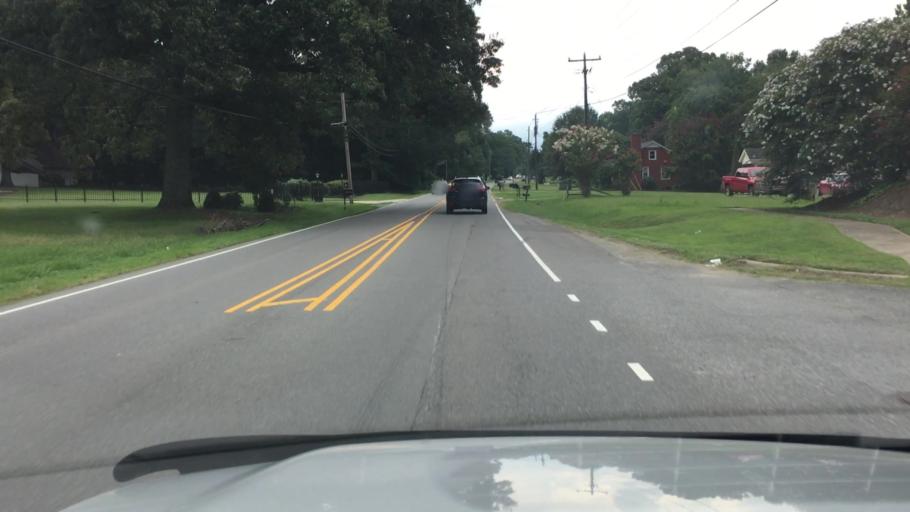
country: US
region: North Carolina
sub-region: Mecklenburg County
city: Huntersville
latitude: 35.3363
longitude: -80.8757
